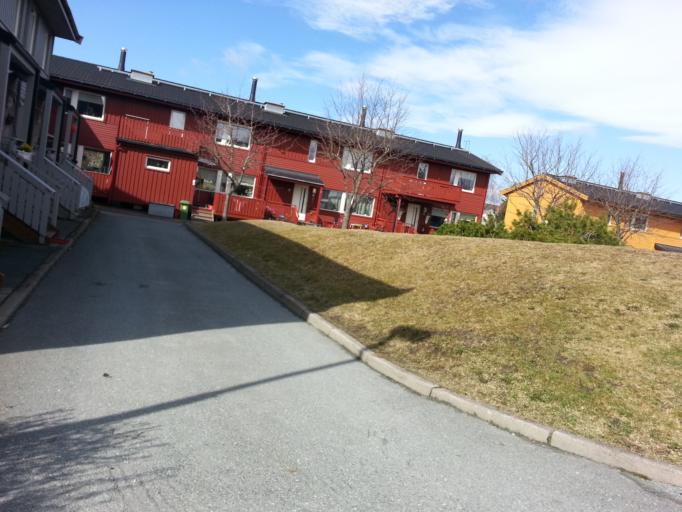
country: NO
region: Sor-Trondelag
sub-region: Trondheim
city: Trondheim
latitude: 63.4282
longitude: 10.4499
